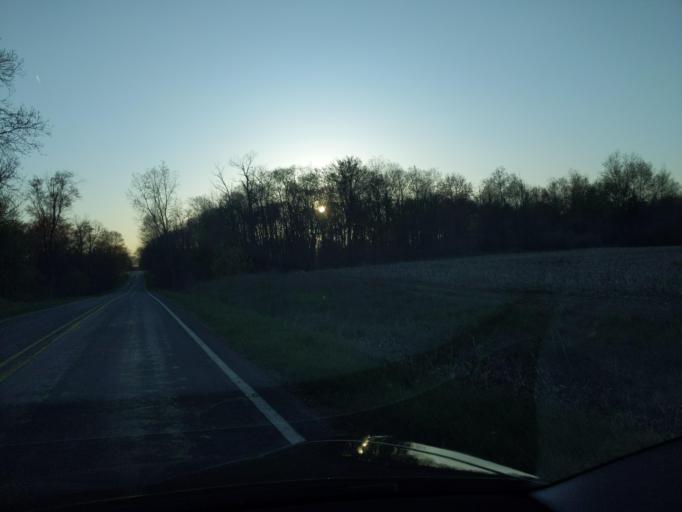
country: US
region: Michigan
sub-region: Ingham County
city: Stockbridge
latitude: 42.4832
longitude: -84.2350
